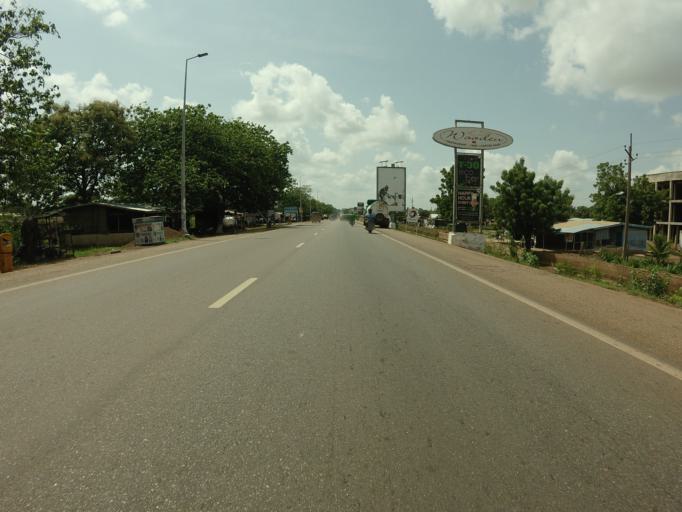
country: GH
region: Northern
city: Tamale
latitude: 9.4403
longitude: -0.8438
